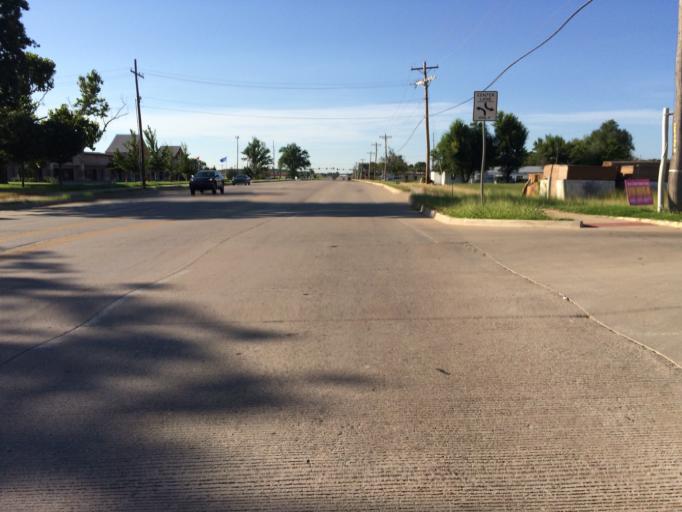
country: US
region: Oklahoma
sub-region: Cleveland County
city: Norman
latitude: 35.1922
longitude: -97.4237
